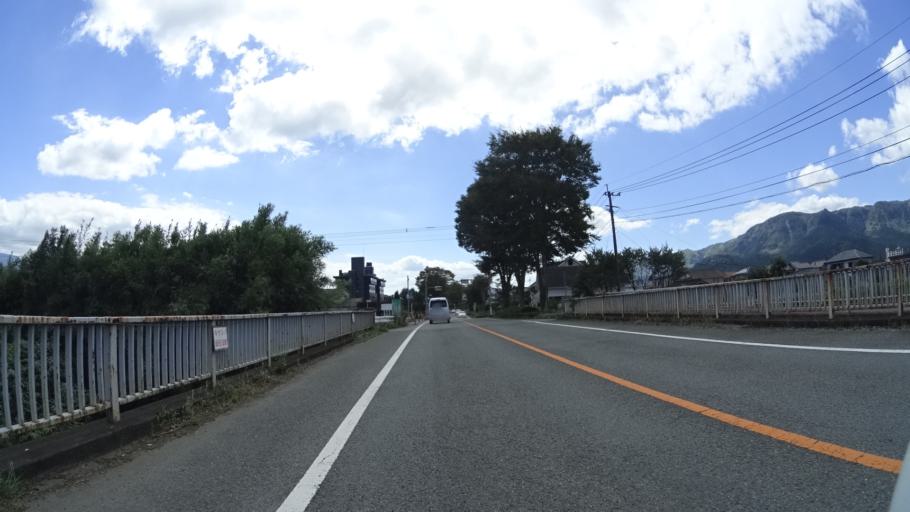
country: JP
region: Kumamoto
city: Aso
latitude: 32.9747
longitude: 131.0514
